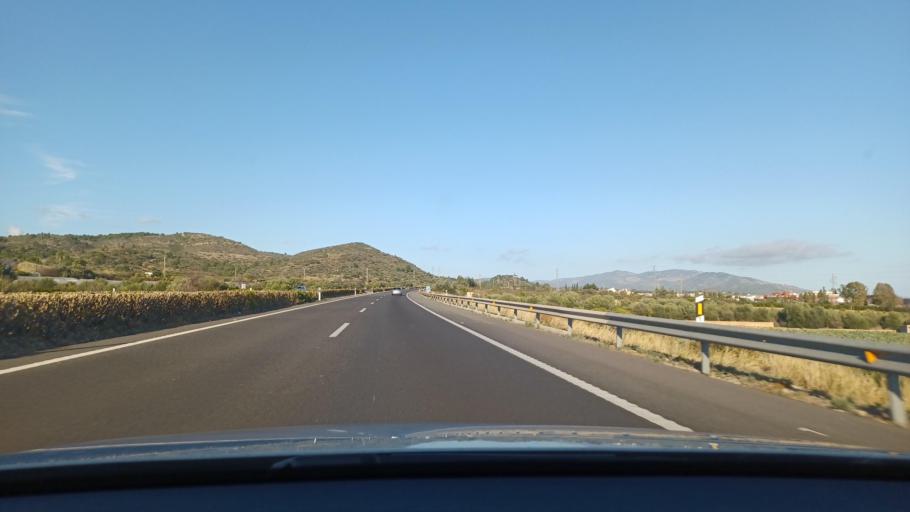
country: ES
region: Valencia
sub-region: Provincia de Castello
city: Torreblanca
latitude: 40.2066
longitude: 0.1772
